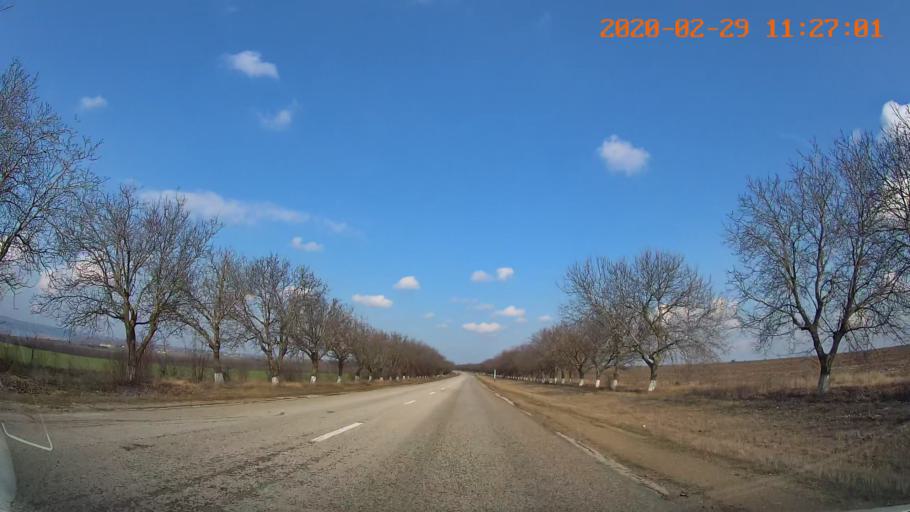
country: MD
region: Telenesti
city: Cocieri
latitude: 47.4617
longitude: 29.1439
